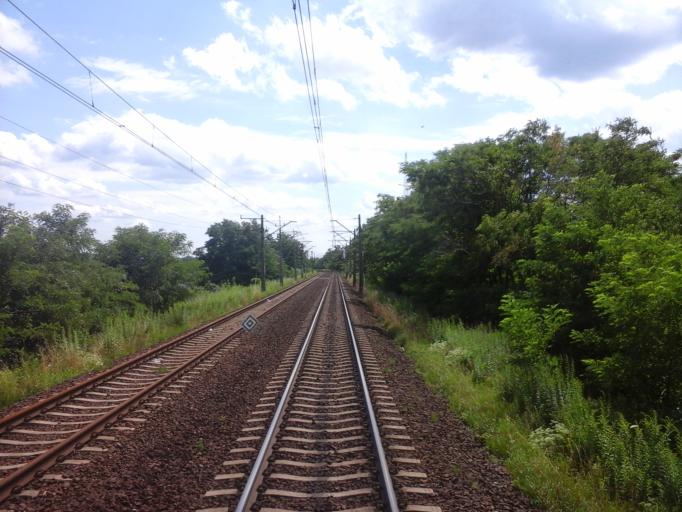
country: PL
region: West Pomeranian Voivodeship
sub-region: Szczecin
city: Szczecin
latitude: 53.3889
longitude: 14.5254
